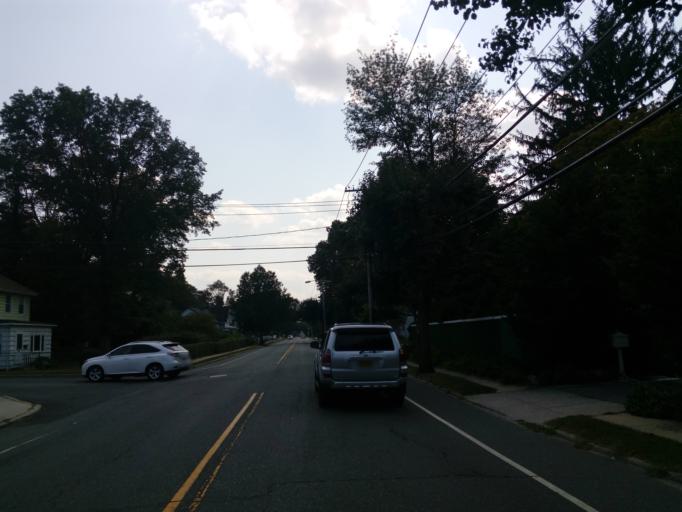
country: US
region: New York
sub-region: Nassau County
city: Glen Cove
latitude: 40.8755
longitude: -73.6307
